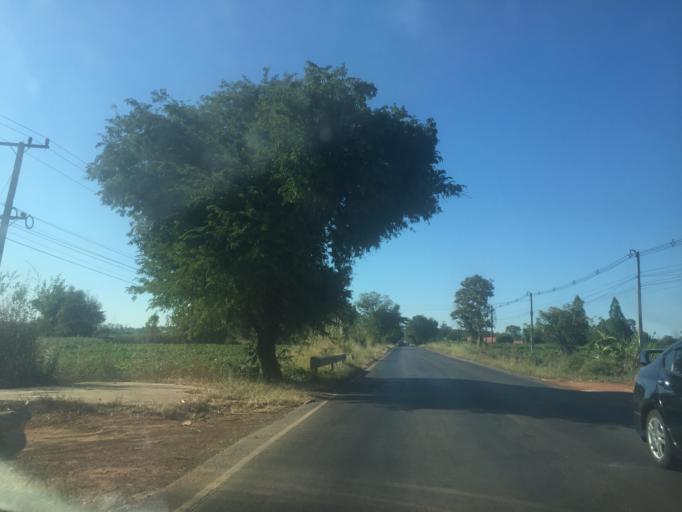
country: TH
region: Kalasin
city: Tha Khantho
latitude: 16.9646
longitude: 103.2470
